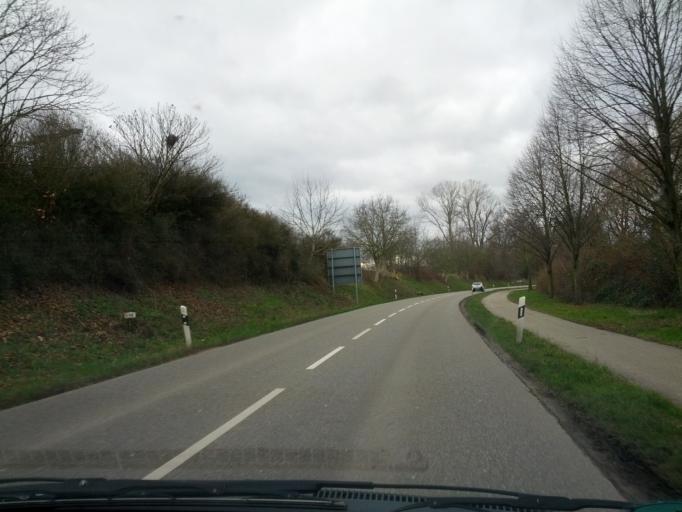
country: DE
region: Baden-Wuerttemberg
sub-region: Freiburg Region
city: Pfaffenweiler
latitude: 47.9212
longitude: 7.7304
